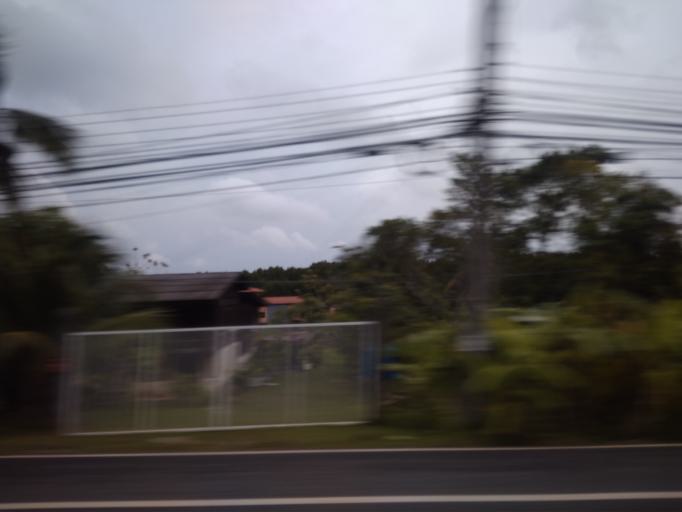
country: TH
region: Phuket
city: Mueang Phuket
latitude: 7.8427
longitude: 98.3858
